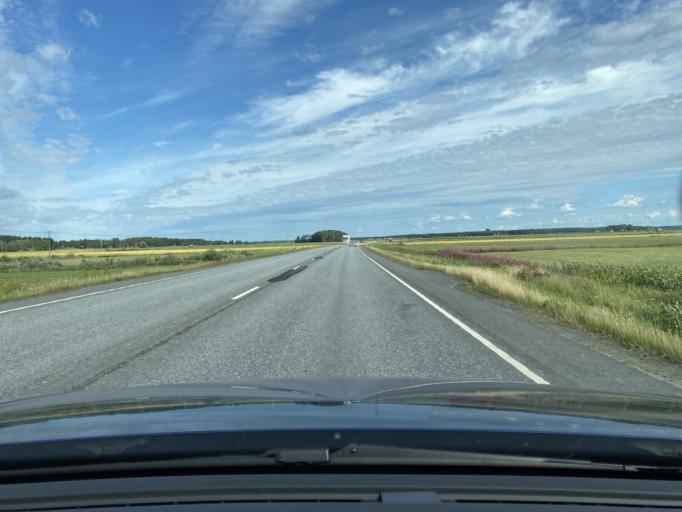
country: FI
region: Southern Ostrobothnia
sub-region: Seinaejoki
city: Ylihaermae
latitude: 63.1837
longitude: 22.8049
